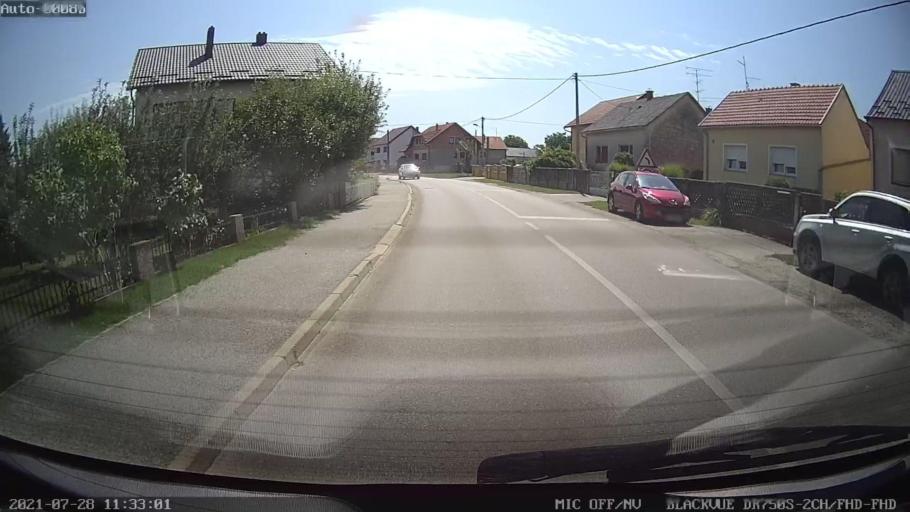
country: HR
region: Medimurska
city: Kursanec
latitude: 46.2832
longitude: 16.3881
